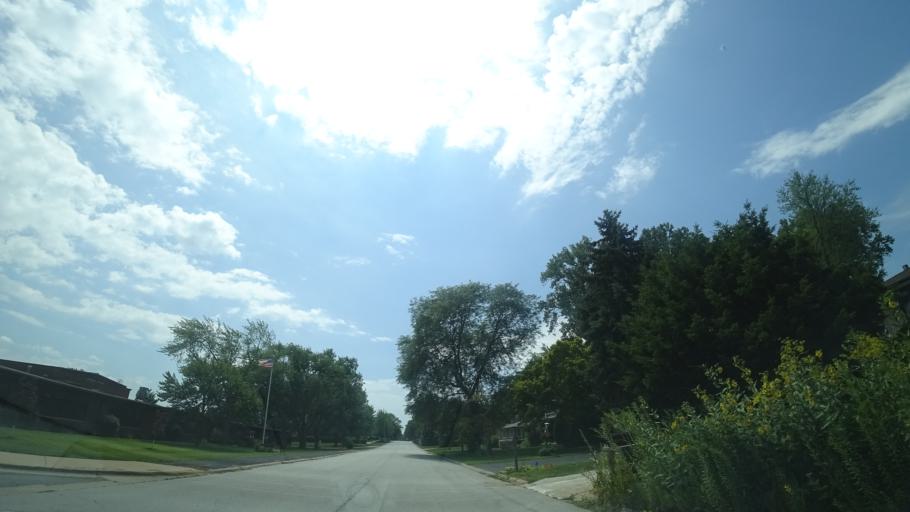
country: US
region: Illinois
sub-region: Cook County
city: Crestwood
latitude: 41.6659
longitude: -87.7683
